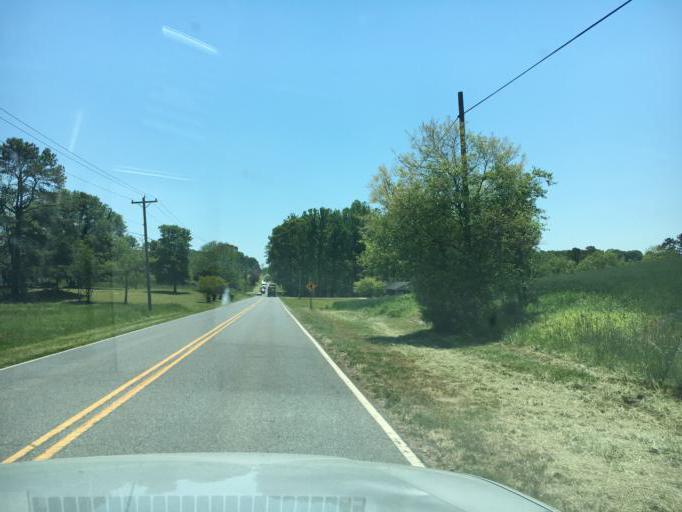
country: US
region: North Carolina
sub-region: Cleveland County
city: Shelby
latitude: 35.3965
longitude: -81.4997
